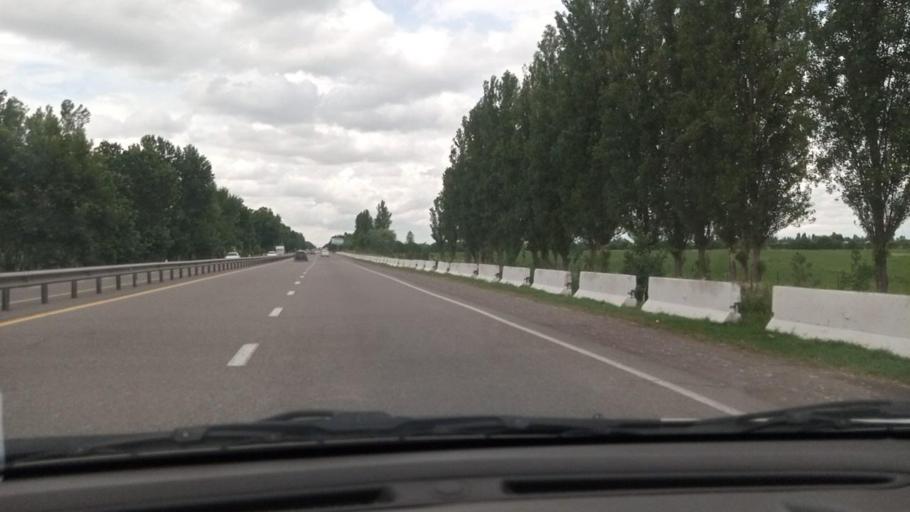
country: UZ
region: Toshkent Shahri
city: Bektemir
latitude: 41.2124
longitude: 69.4028
